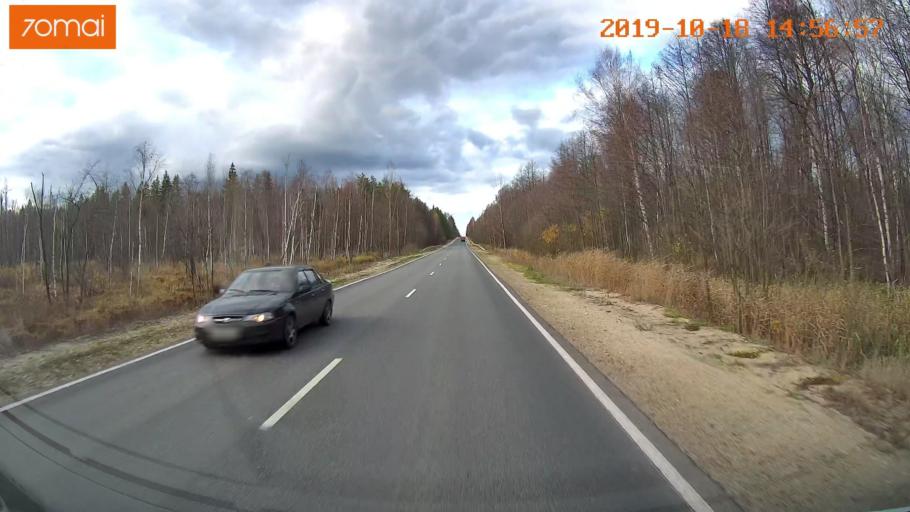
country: RU
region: Vladimir
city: Kurlovo
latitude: 55.4724
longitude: 40.5845
